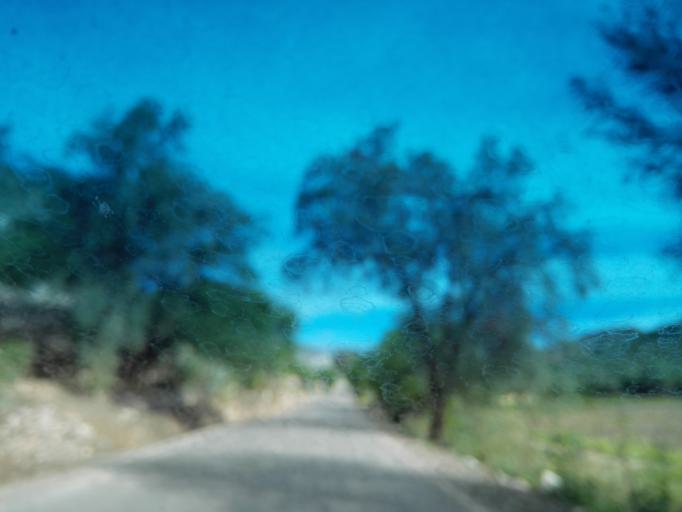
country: PE
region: Ayacucho
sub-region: Provincia de Huamanga
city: Pacaycasa
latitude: -13.0785
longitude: -74.2316
